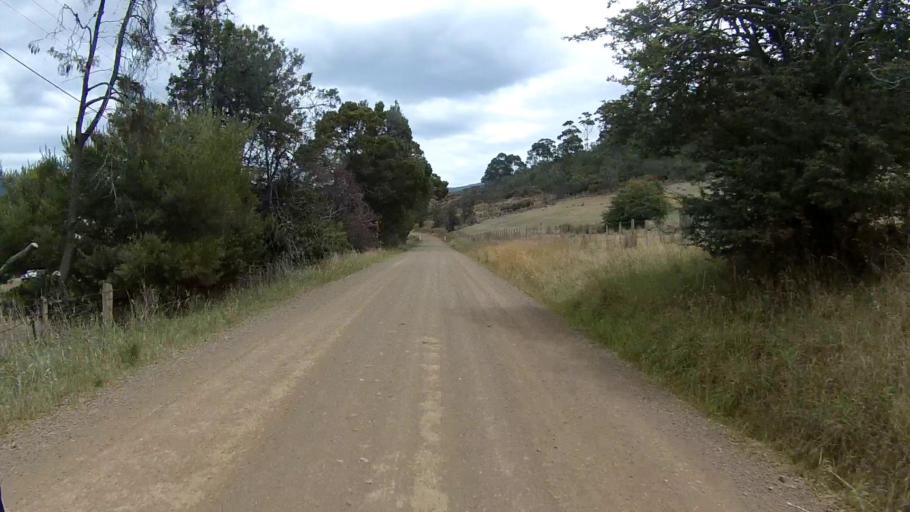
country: AU
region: Tasmania
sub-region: Sorell
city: Sorell
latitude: -42.6283
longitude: 147.9310
